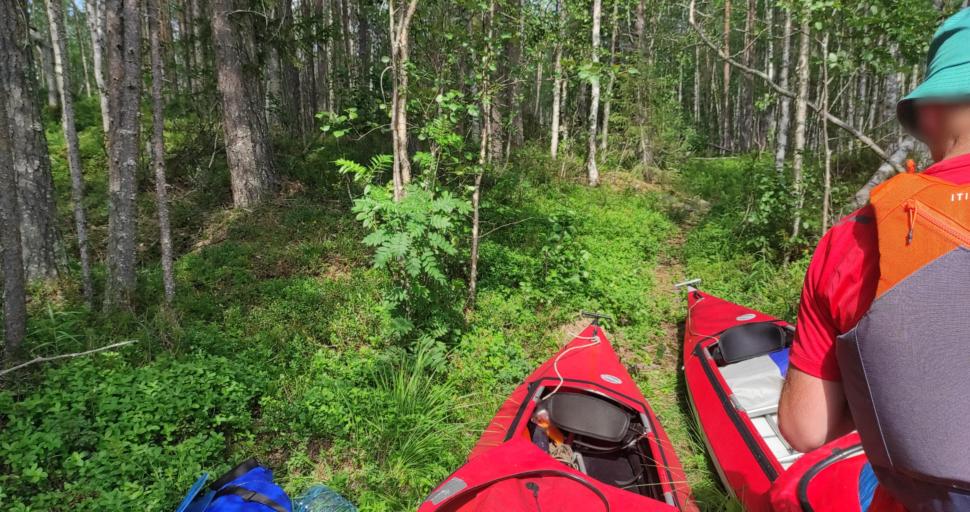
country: RU
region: Murmansk
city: Zelenoborskiy
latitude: 66.7120
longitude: 32.4516
